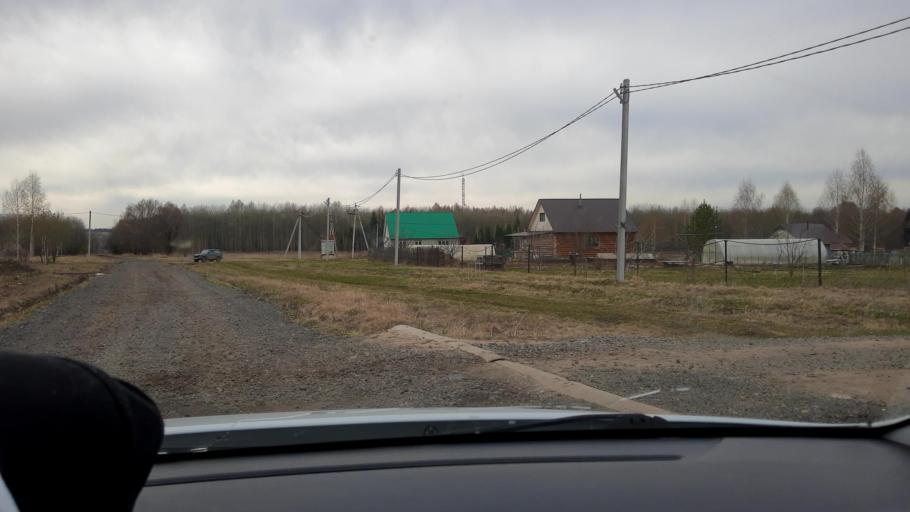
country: RU
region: Bashkortostan
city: Iglino
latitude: 54.7683
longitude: 56.5229
